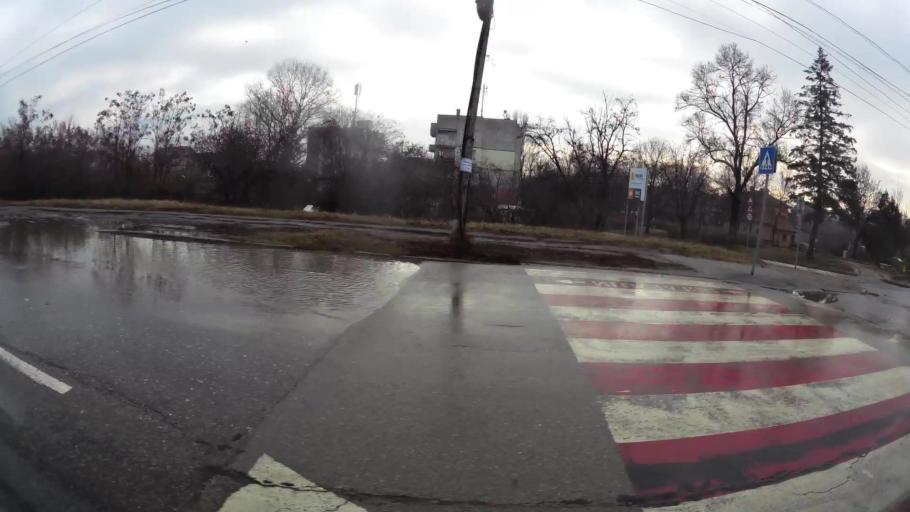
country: BG
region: Sofia-Capital
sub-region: Stolichna Obshtina
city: Sofia
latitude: 42.7383
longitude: 23.3436
